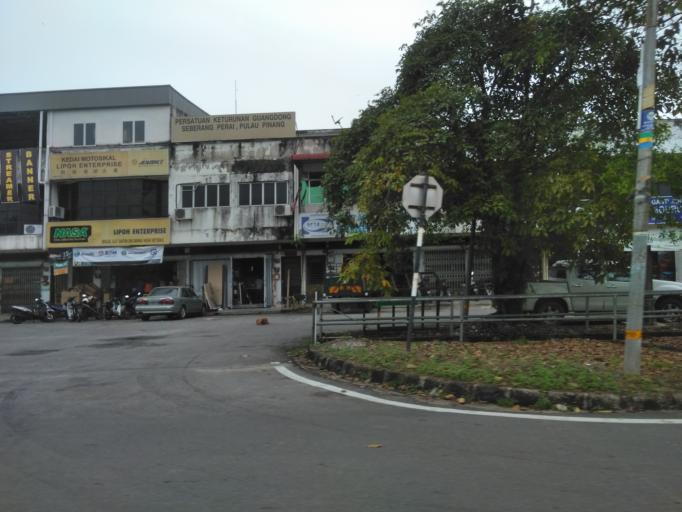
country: MY
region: Penang
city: Perai
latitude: 5.4107
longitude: 100.4166
